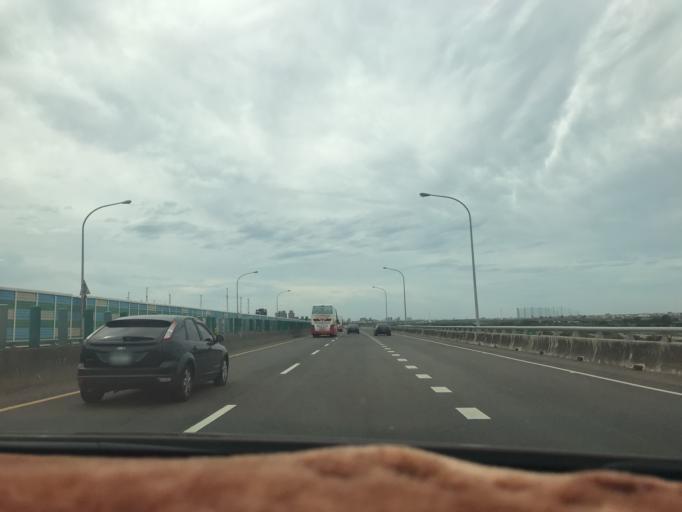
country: TW
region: Taiwan
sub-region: Hsinchu
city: Zhubei
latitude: 24.8210
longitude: 120.9919
